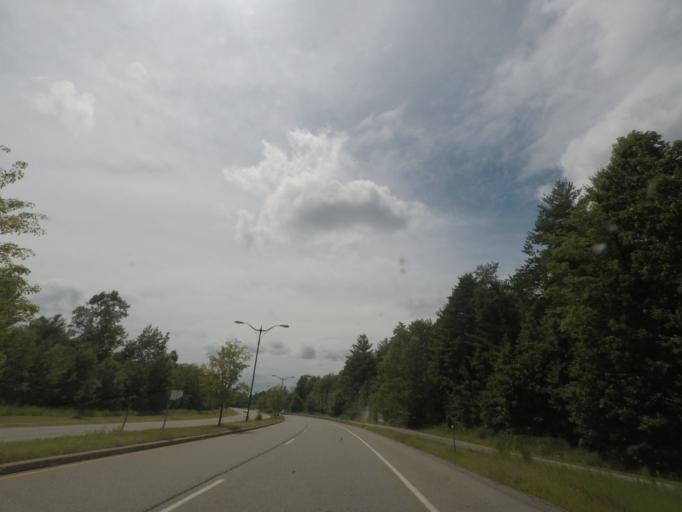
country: US
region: New York
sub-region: Saratoga County
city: Country Knolls
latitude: 42.9564
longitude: -73.7643
